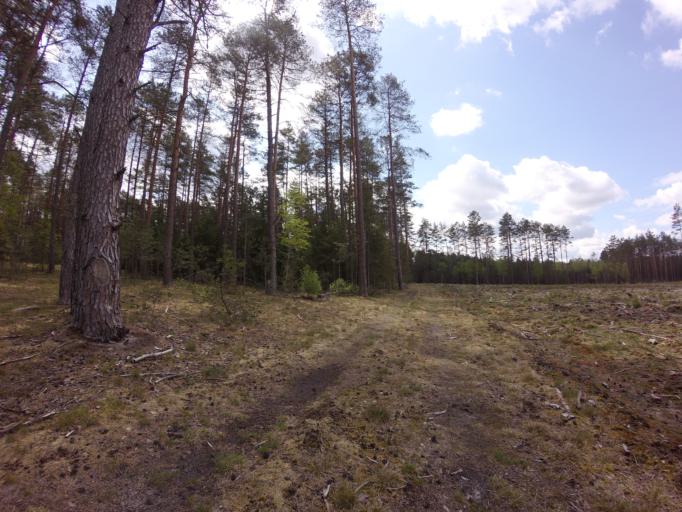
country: PL
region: West Pomeranian Voivodeship
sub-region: Powiat drawski
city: Kalisz Pomorski
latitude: 53.1957
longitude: 16.0019
